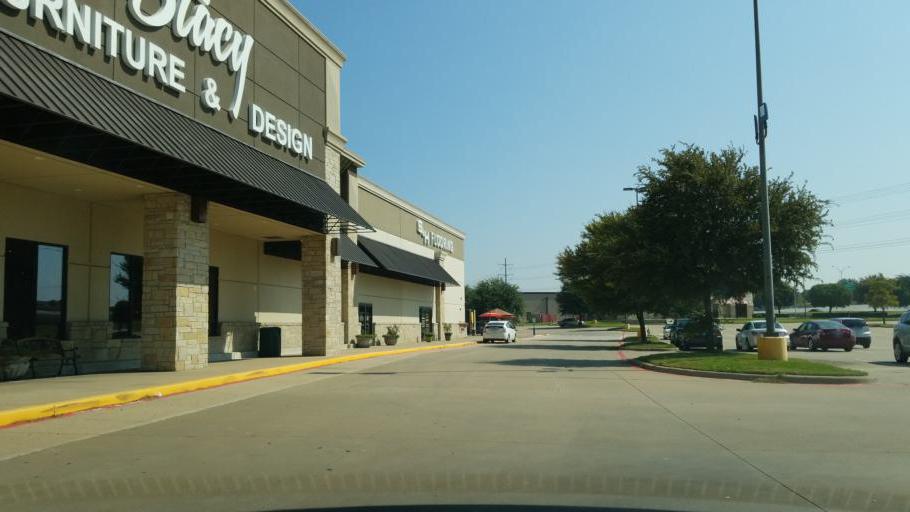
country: US
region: Texas
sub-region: Collin County
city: Allen
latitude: 33.1040
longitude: -96.6791
